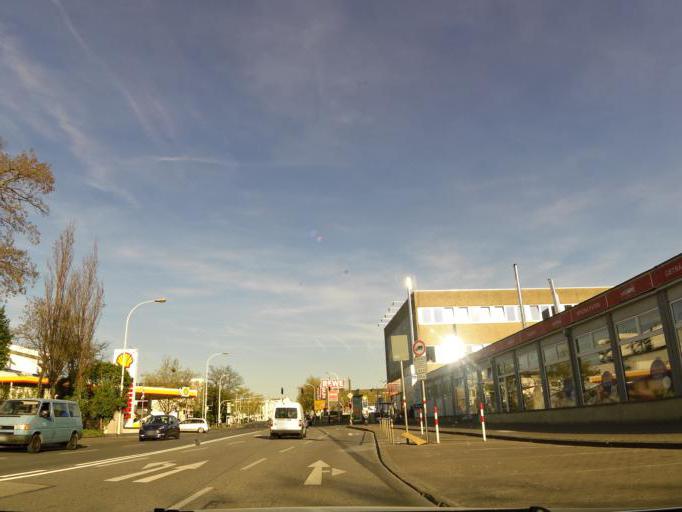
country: DE
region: Hesse
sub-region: Regierungsbezirk Darmstadt
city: Darmstadt
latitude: 49.8825
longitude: 8.6420
